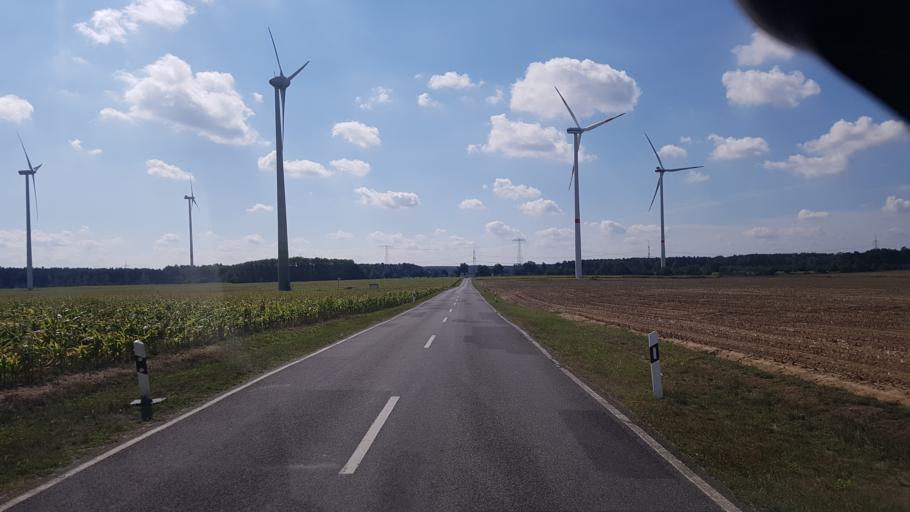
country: DE
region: Brandenburg
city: Drebkau
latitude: 51.6605
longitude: 14.2826
